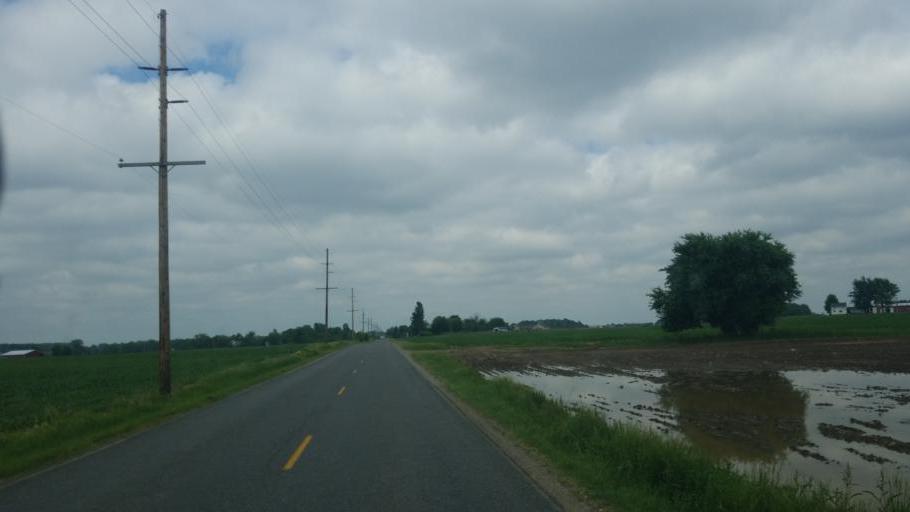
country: US
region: Indiana
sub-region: Elkhart County
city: Nappanee
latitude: 41.4811
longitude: -86.0457
